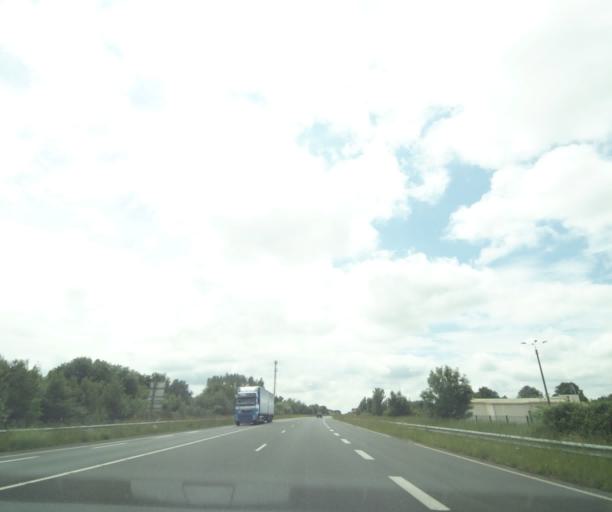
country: FR
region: Poitou-Charentes
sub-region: Departement des Deux-Sevres
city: Saint-Pardoux
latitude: 46.5435
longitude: -0.3129
